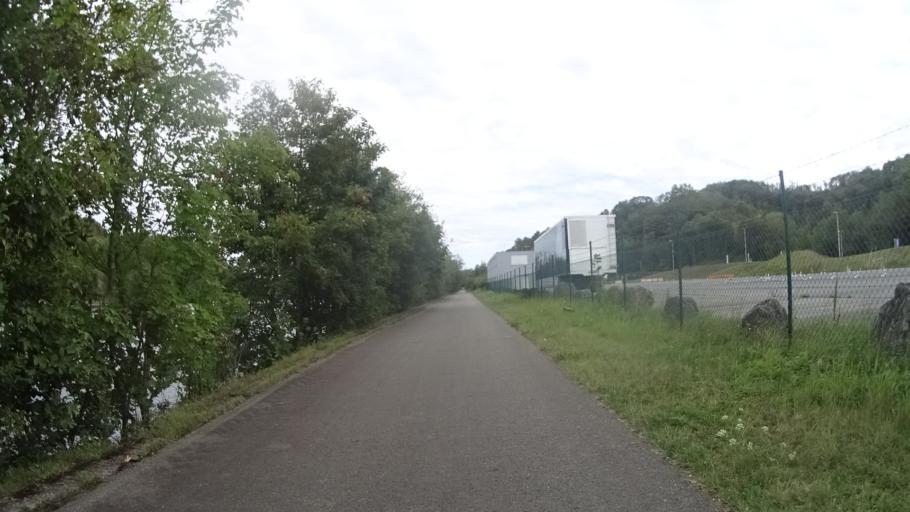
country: BE
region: Wallonia
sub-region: Province de Namur
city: Andenne
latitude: 50.4951
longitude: 5.0553
